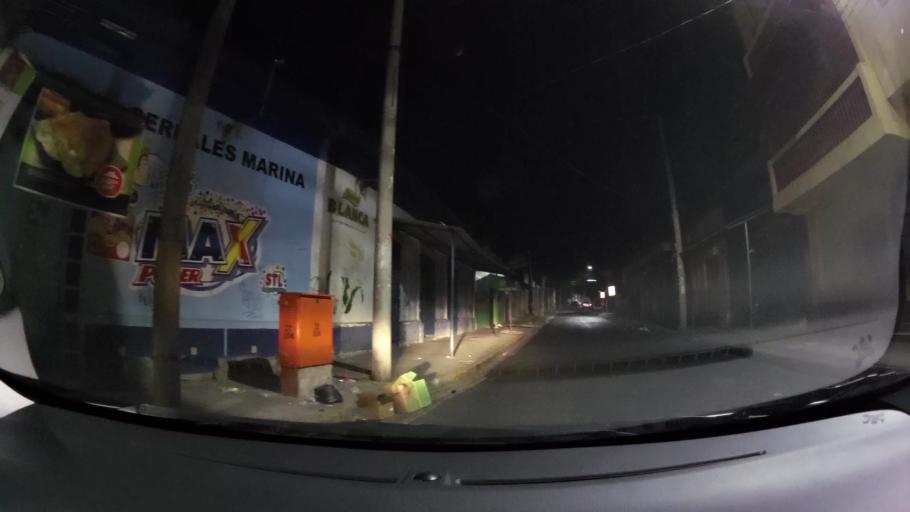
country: SV
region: La Paz
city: Zacatecoluca
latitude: 13.5086
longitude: -88.8683
